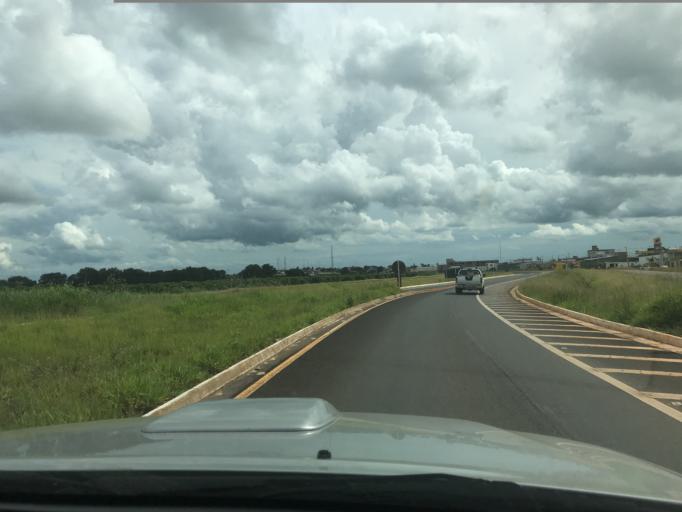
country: BR
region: Minas Gerais
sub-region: Patrocinio
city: Patrocinio
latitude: -19.0979
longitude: -46.6740
